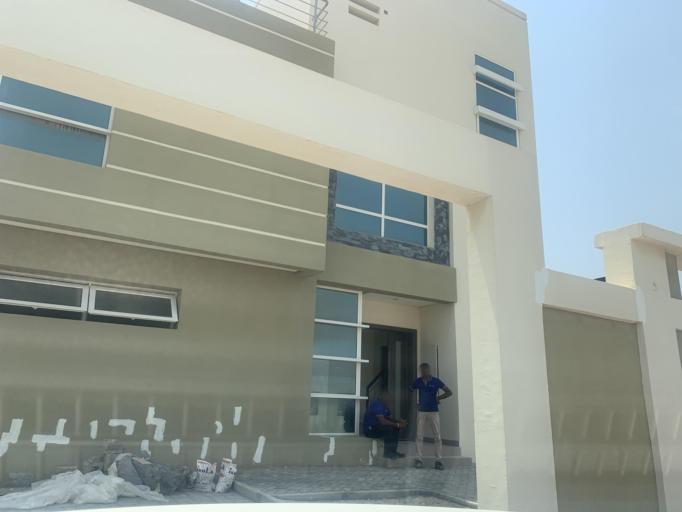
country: BH
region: Central Governorate
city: Madinat Hamad
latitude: 26.1366
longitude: 50.4661
